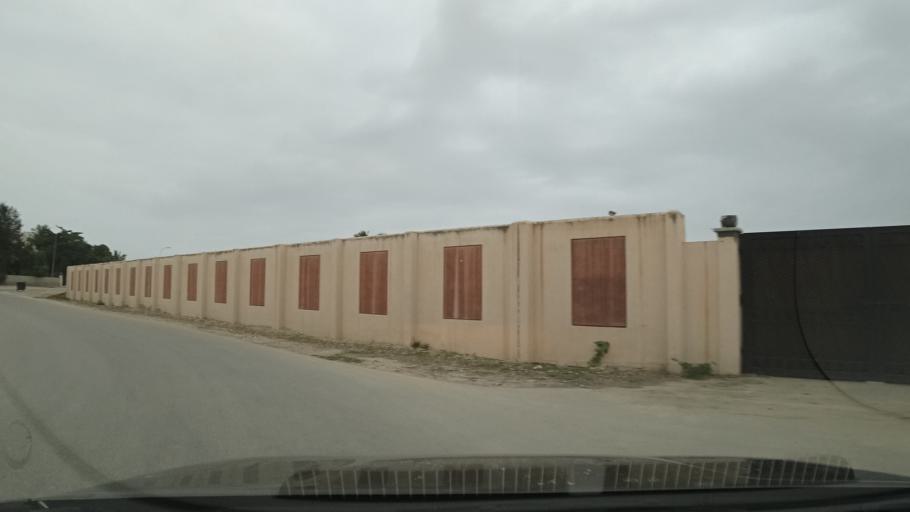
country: OM
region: Zufar
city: Salalah
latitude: 17.0248
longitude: 54.1529
